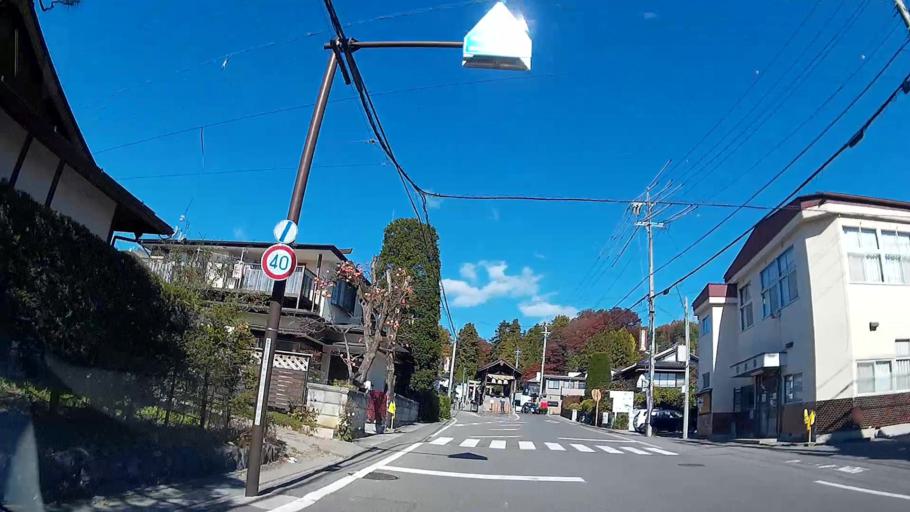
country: JP
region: Nagano
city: Okaya
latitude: 36.0797
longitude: 138.0818
